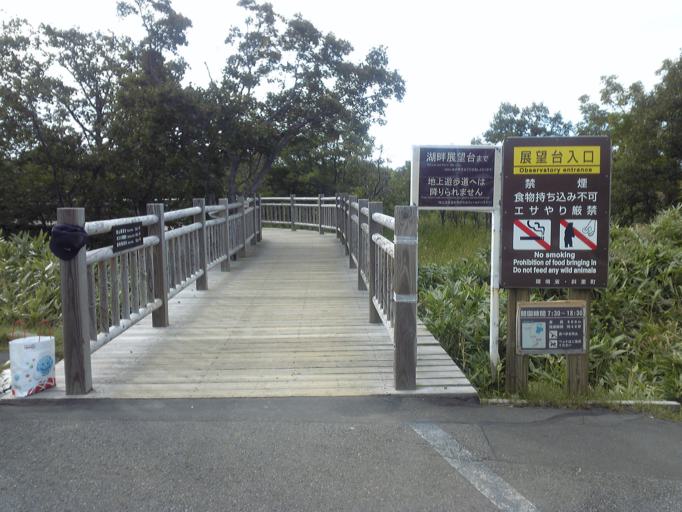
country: JP
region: Hokkaido
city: Shibetsu
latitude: 44.1221
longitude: 145.0801
